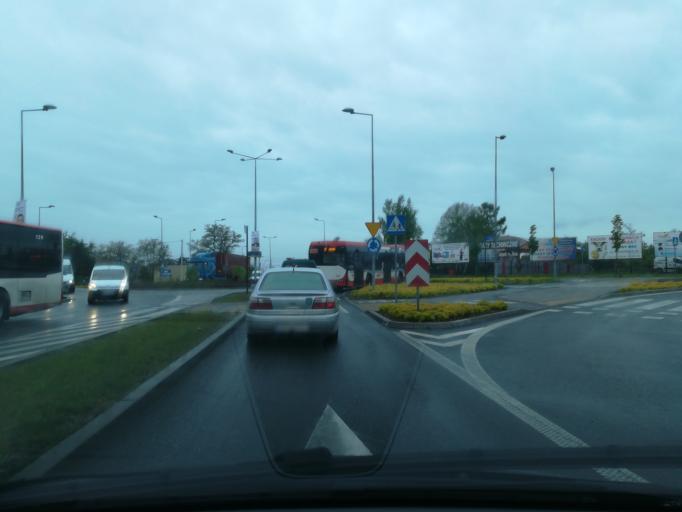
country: PL
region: Silesian Voivodeship
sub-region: Czestochowa
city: Czestochowa
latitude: 50.8339
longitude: 19.1510
